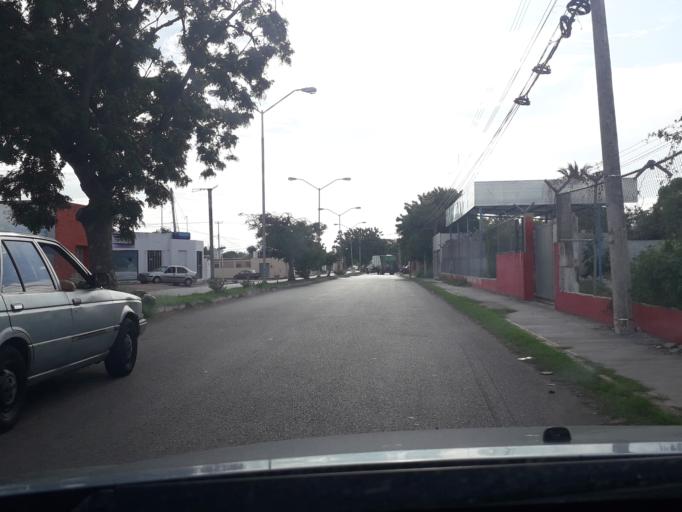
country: MX
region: Yucatan
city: Merida
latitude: 21.0019
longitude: -89.6403
